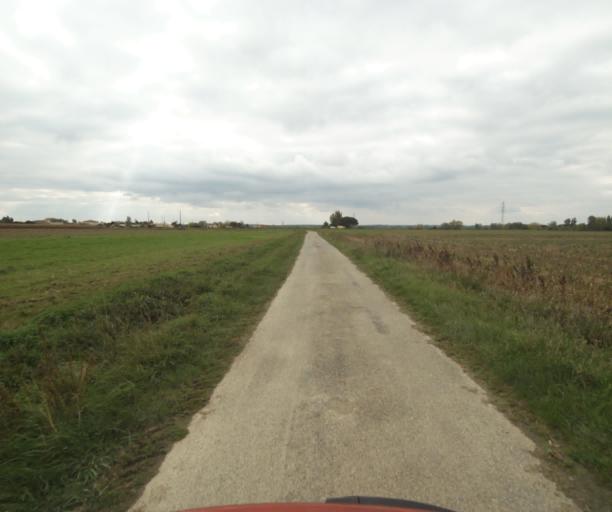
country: FR
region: Midi-Pyrenees
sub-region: Departement du Tarn-et-Garonne
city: Verdun-sur-Garonne
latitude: 43.8887
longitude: 1.2512
